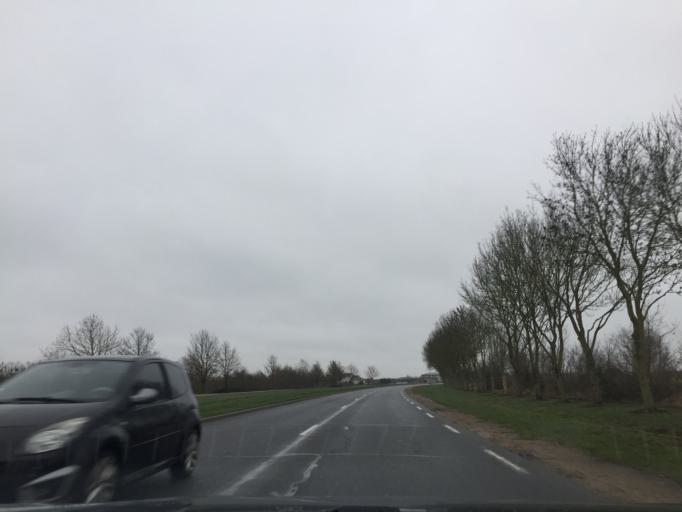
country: FR
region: Ile-de-France
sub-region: Departement de Seine-et-Marne
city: Magny-le-Hongre
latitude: 48.8726
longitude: 2.8045
